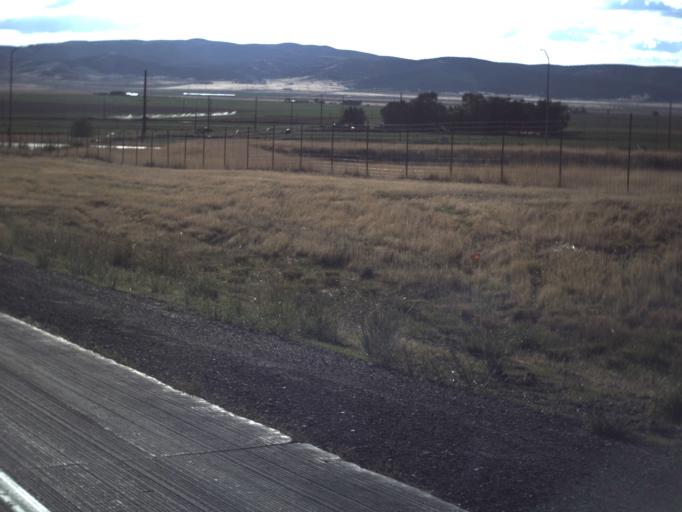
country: US
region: Utah
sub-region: Juab County
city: Nephi
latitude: 39.6838
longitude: -111.8366
